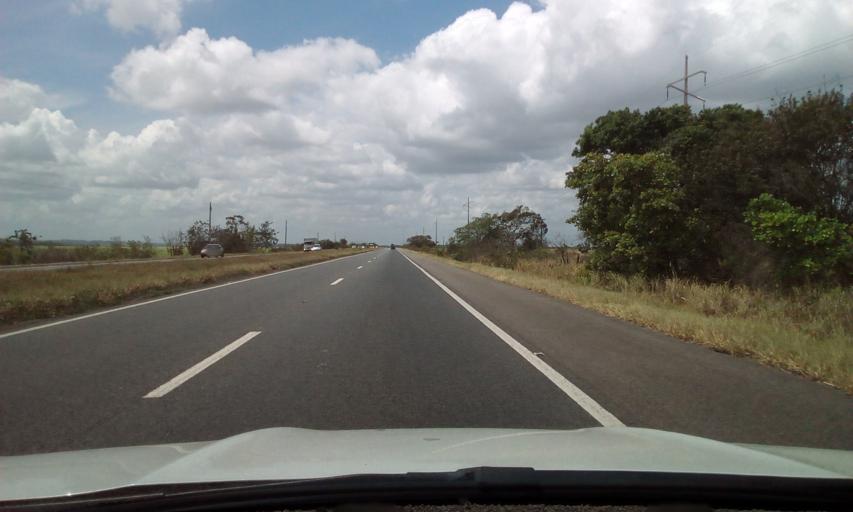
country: BR
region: Paraiba
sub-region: Cruz Do Espirito Santo
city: Cruz do Espirito Santo
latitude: -7.1838
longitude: -35.0533
